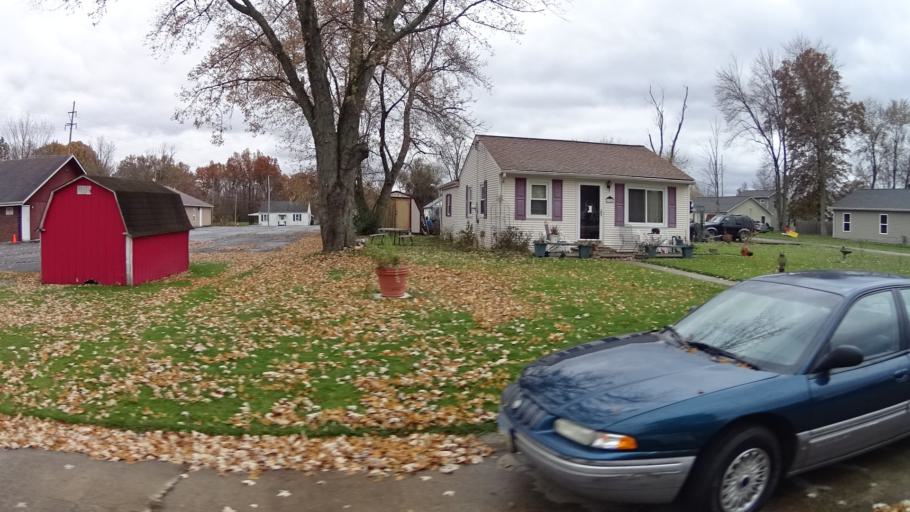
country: US
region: Ohio
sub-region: Lorain County
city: Elyria
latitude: 41.3497
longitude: -82.1219
